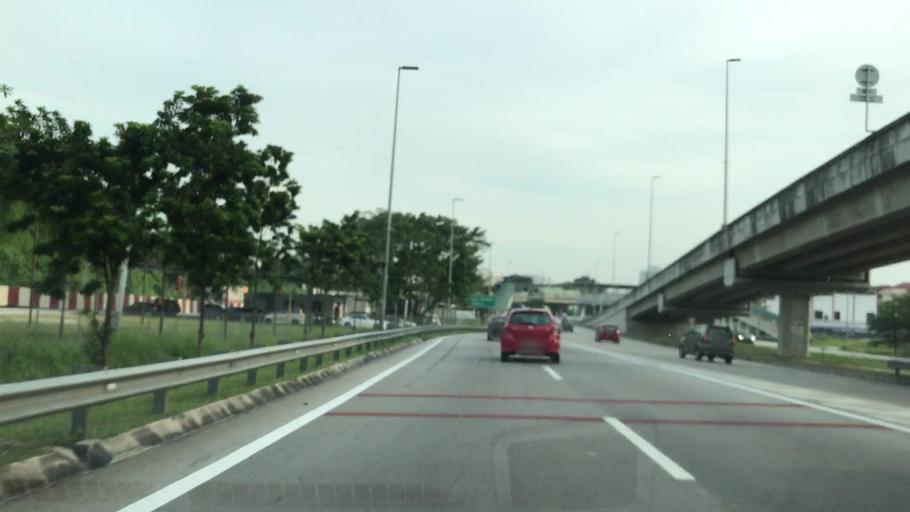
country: MY
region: Kuala Lumpur
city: Kuala Lumpur
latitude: 3.1080
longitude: 101.7075
